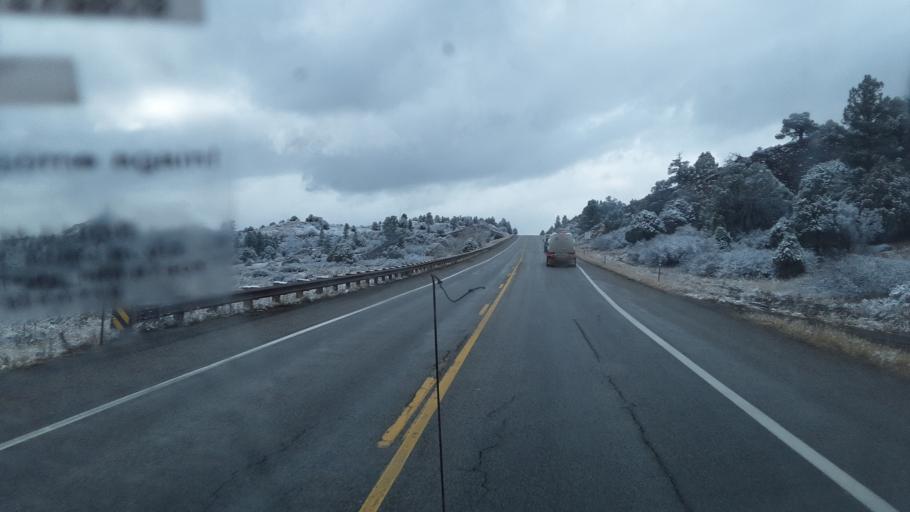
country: US
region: Colorado
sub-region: Archuleta County
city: Pagosa Springs
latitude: 37.2083
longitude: -107.2509
